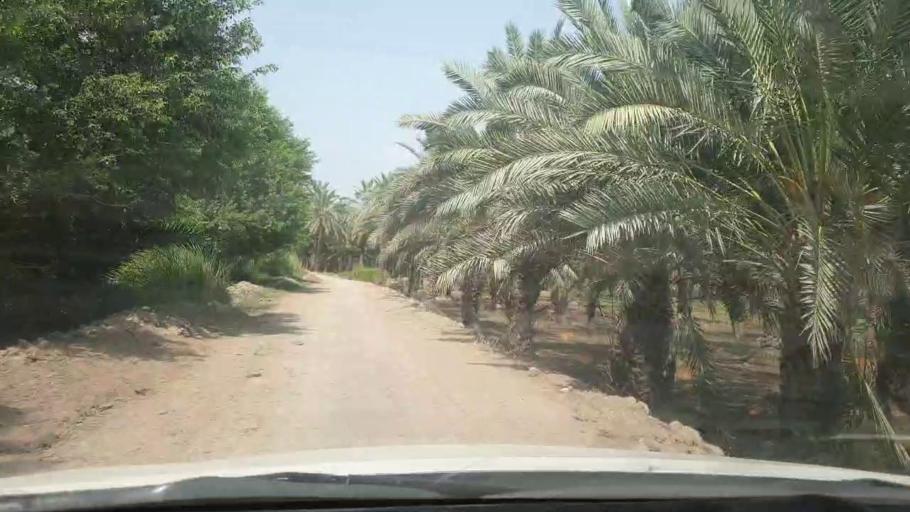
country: PK
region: Sindh
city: Khairpur
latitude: 27.5541
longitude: 68.8400
